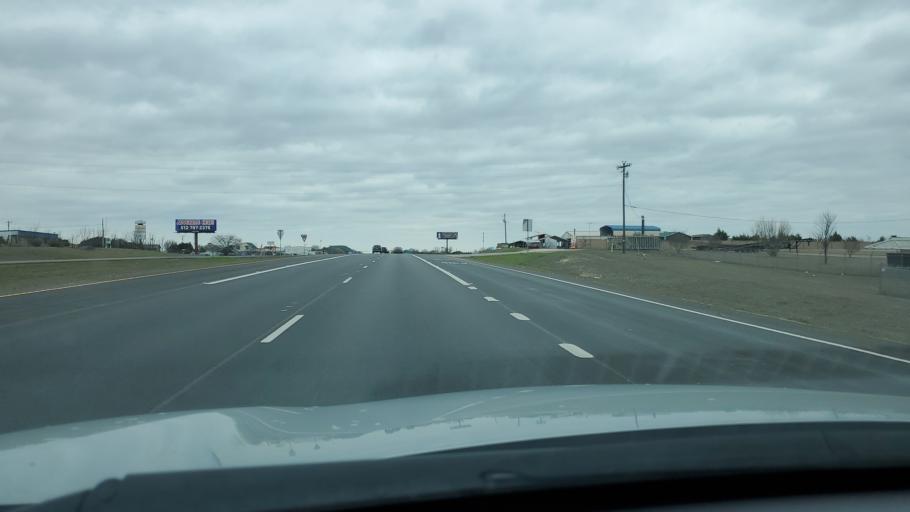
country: US
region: Texas
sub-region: Bell County
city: Killeen
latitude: 31.0148
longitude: -97.7526
